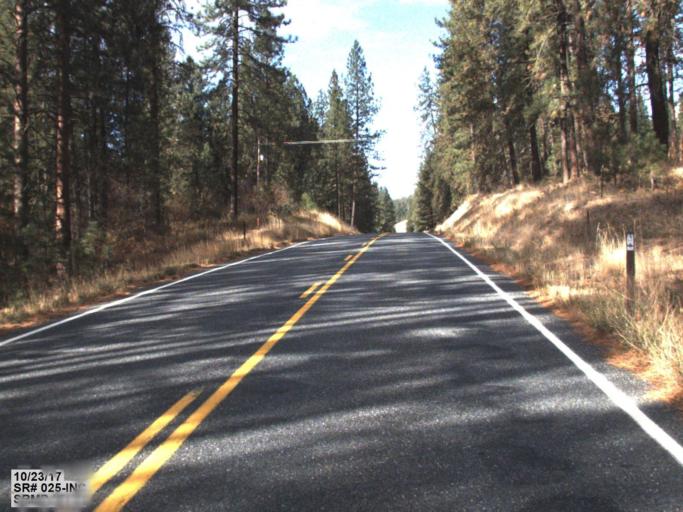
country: US
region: Washington
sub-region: Stevens County
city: Kettle Falls
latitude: 48.2712
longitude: -118.1338
